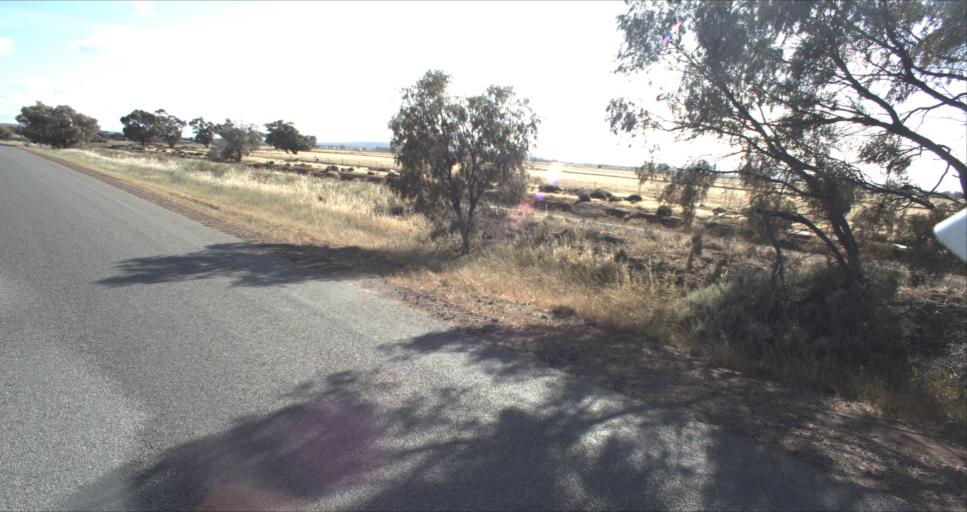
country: AU
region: New South Wales
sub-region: Leeton
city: Leeton
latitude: -34.5143
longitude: 146.3918
